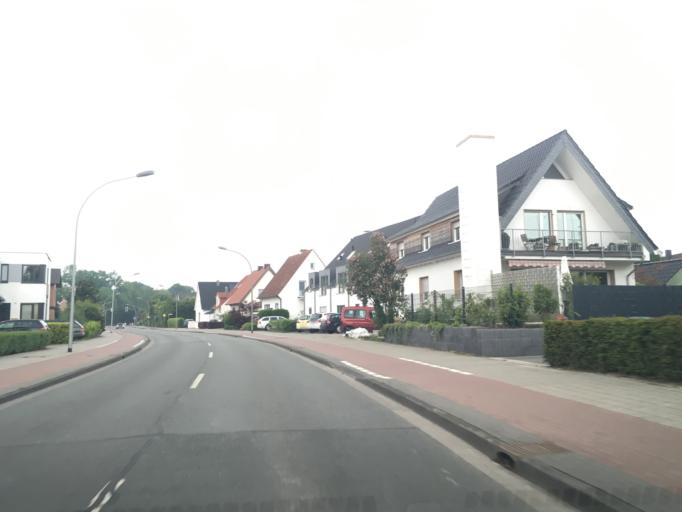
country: DE
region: North Rhine-Westphalia
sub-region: Regierungsbezirk Munster
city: Muenster
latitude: 51.9508
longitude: 7.6765
